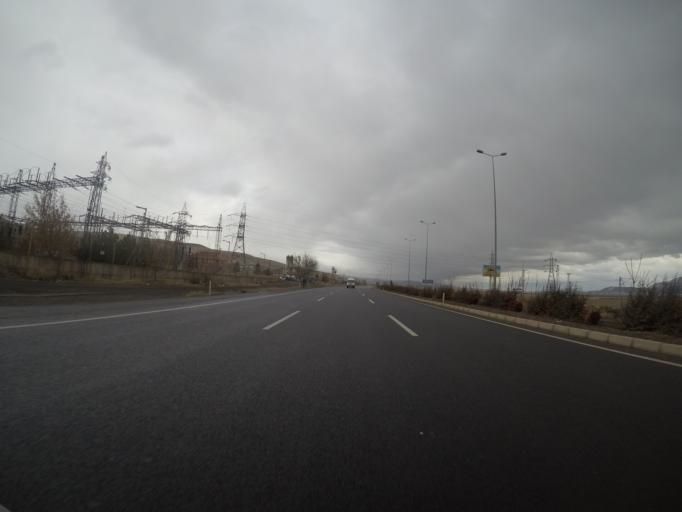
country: TR
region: Kayseri
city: Incesu
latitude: 38.7165
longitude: 35.2686
